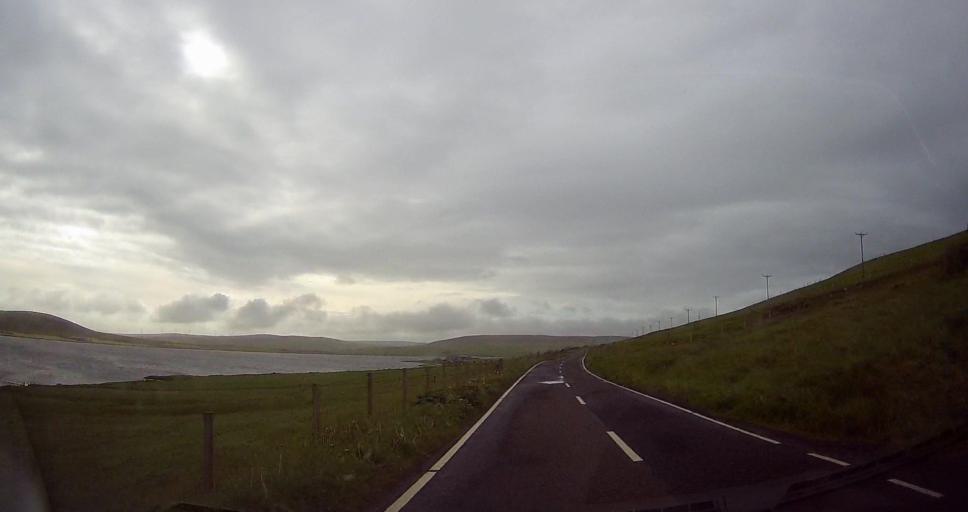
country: GB
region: Scotland
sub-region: Orkney Islands
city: Stromness
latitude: 59.1119
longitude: -3.2943
